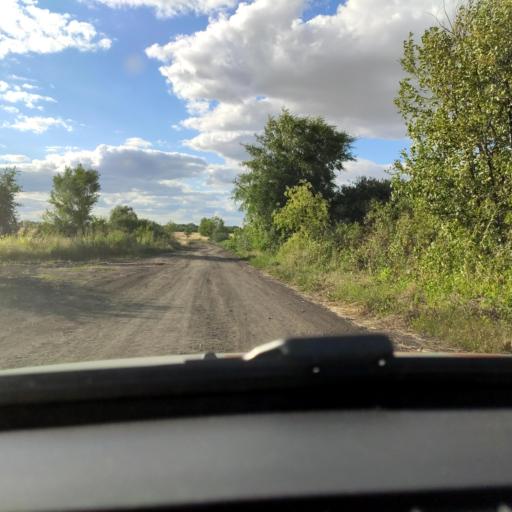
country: RU
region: Voronezj
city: Verkhnyaya Khava
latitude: 51.6065
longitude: 39.8367
